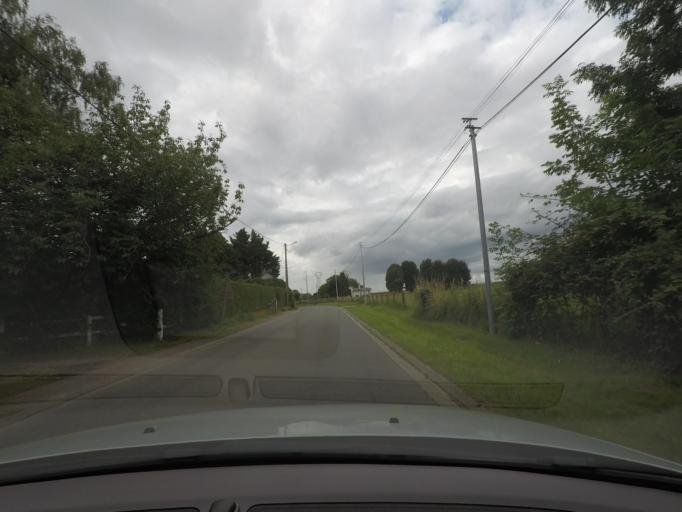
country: FR
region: Haute-Normandie
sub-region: Departement de l'Eure
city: Fleury-sur-Andelle
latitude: 49.2888
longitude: 1.3389
